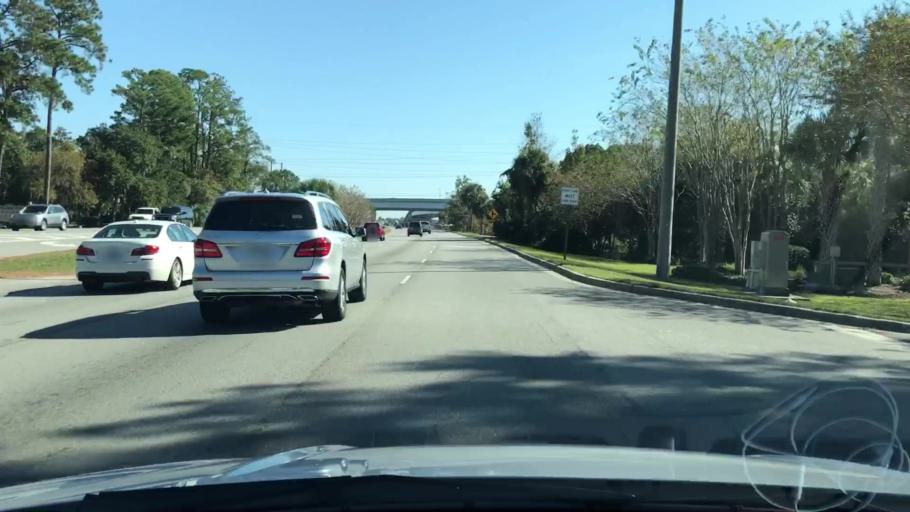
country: US
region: South Carolina
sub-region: Beaufort County
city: Bluffton
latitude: 32.2357
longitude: -80.8064
